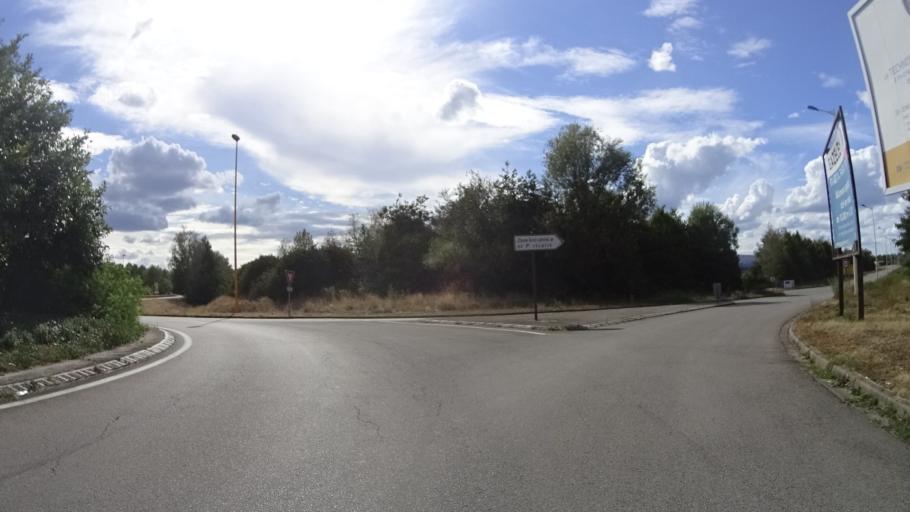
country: FR
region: Bourgogne
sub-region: Departement de la Cote-d'Or
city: Seurre
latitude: 47.0357
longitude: 5.1798
